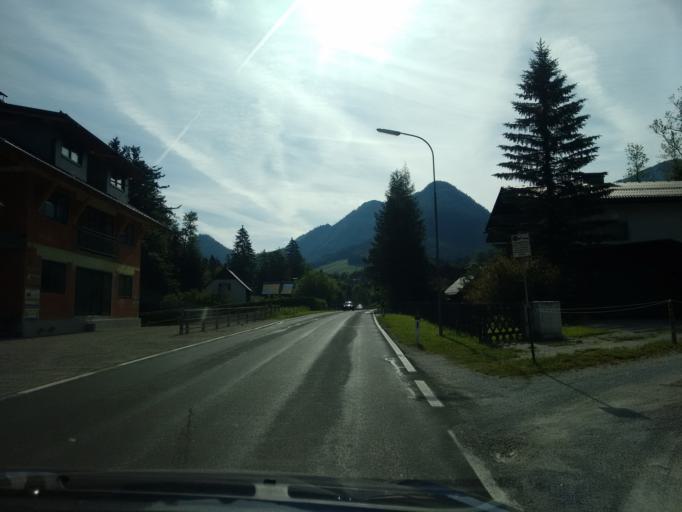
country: AT
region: Styria
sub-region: Politischer Bezirk Liezen
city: Bad Aussee
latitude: 47.6163
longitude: 13.8133
